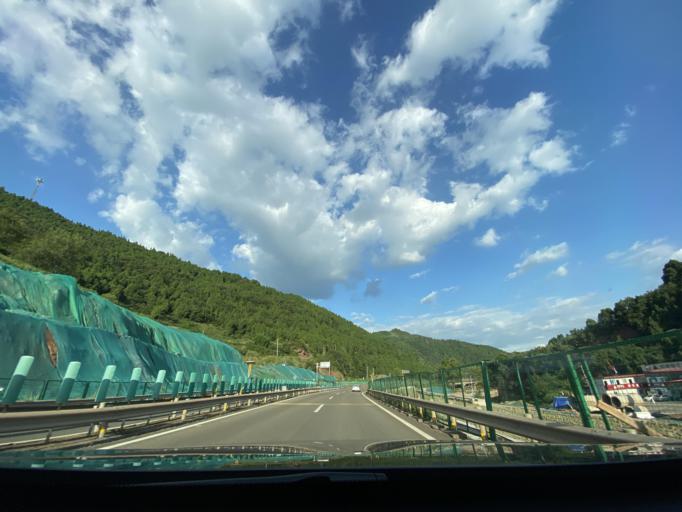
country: CN
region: Sichuan
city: Longquan
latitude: 30.5586
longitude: 104.3458
